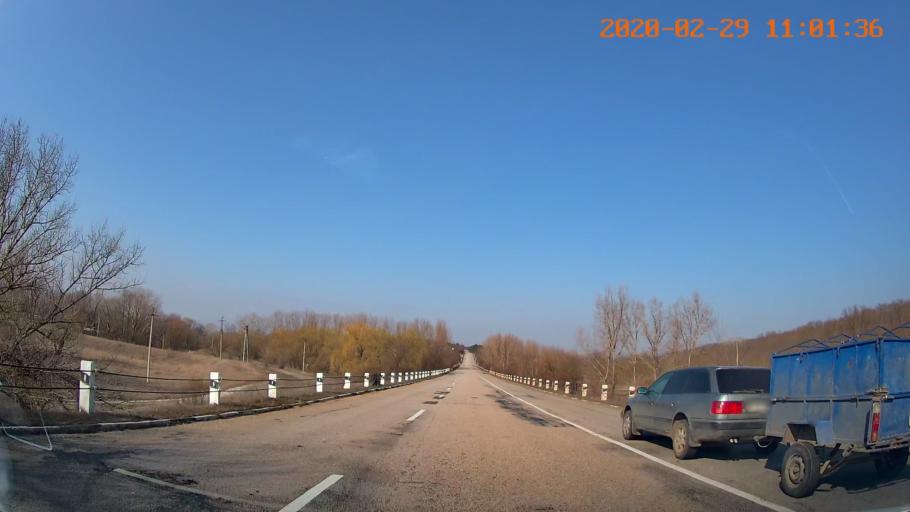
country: MD
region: Telenesti
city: Grigoriopol
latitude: 47.1653
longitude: 29.2553
